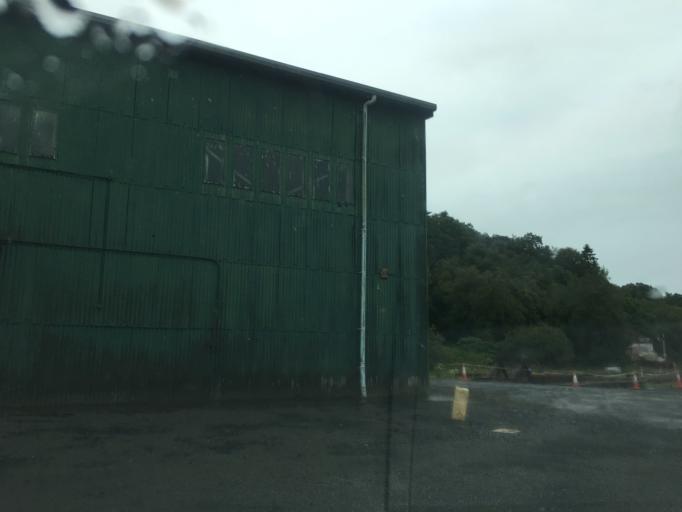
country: GB
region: Scotland
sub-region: Fife
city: Townhill
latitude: 56.1115
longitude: -3.4614
